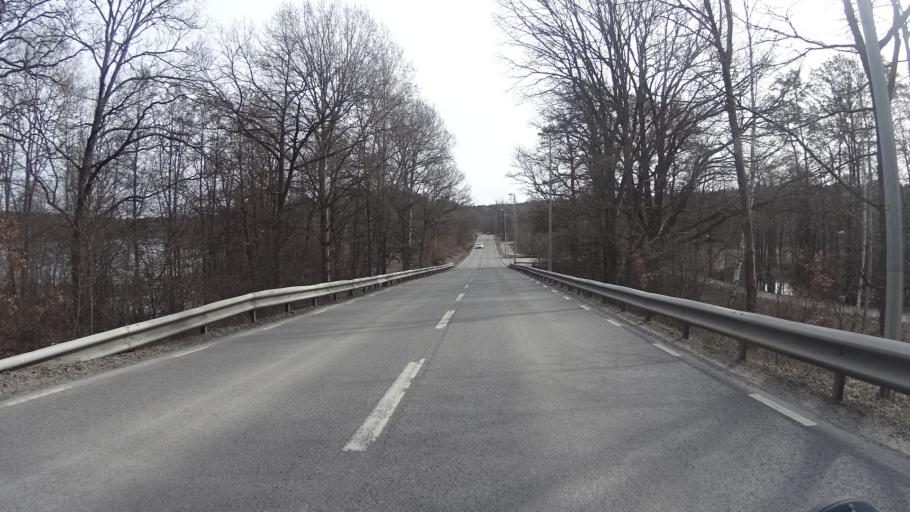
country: SE
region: Stockholm
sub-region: Nacka Kommun
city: Nacka
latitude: 59.2910
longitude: 18.1531
